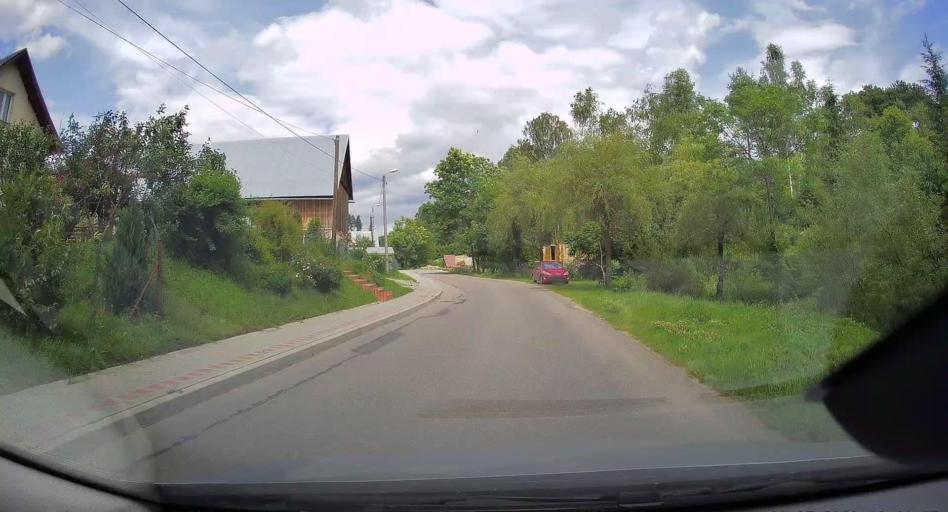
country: PL
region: Lesser Poland Voivodeship
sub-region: Powiat nowosadecki
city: Muszyna
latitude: 49.3801
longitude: 20.8946
